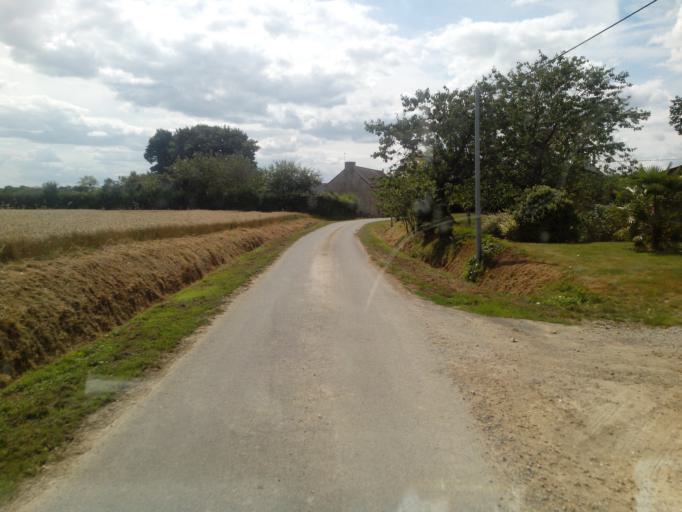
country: FR
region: Brittany
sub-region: Departement du Morbihan
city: Guilliers
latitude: 48.1034
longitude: -2.4035
